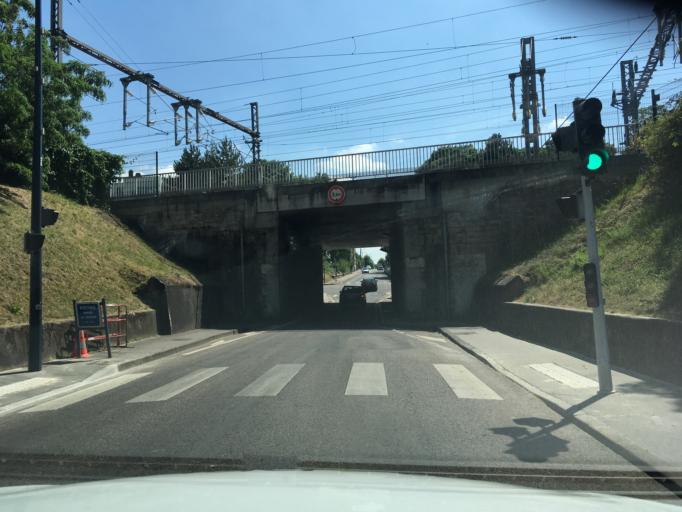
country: FR
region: Lorraine
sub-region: Departement de Meurthe-et-Moselle
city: Jarville-la-Malgrange
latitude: 48.6714
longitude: 6.2008
